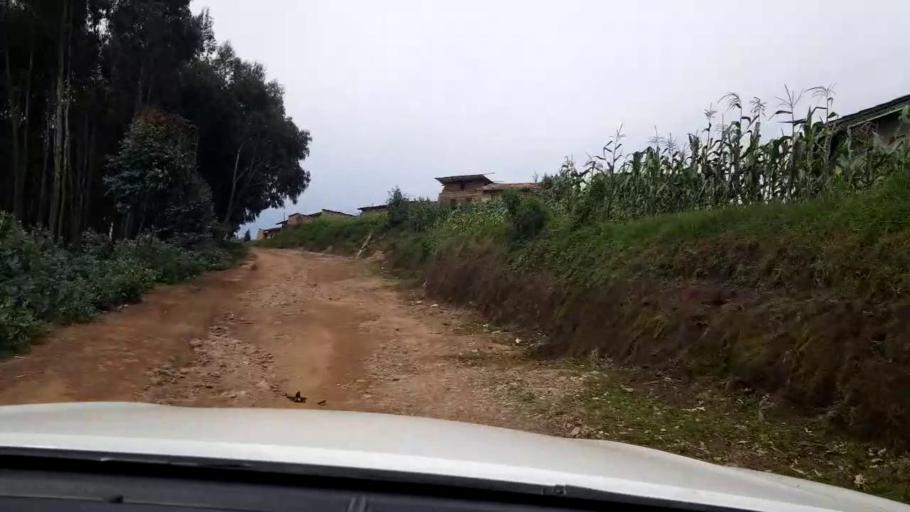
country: RW
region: Western Province
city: Kibuye
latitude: -1.8800
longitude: 29.4551
